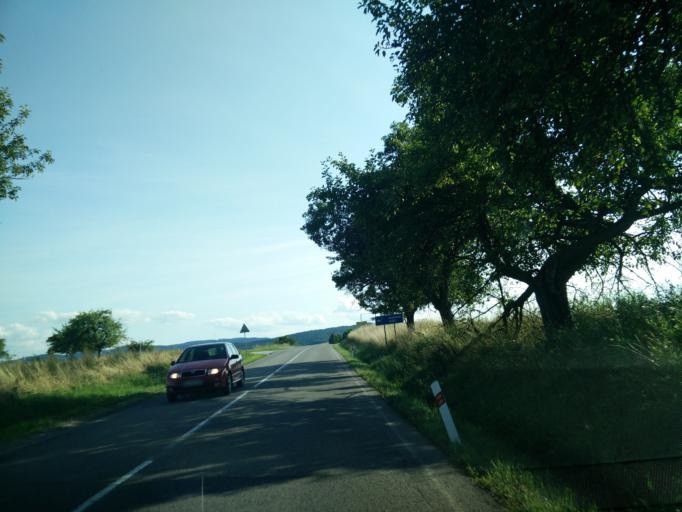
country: SK
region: Nitriansky
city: Handlova
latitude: 48.8913
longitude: 18.7520
